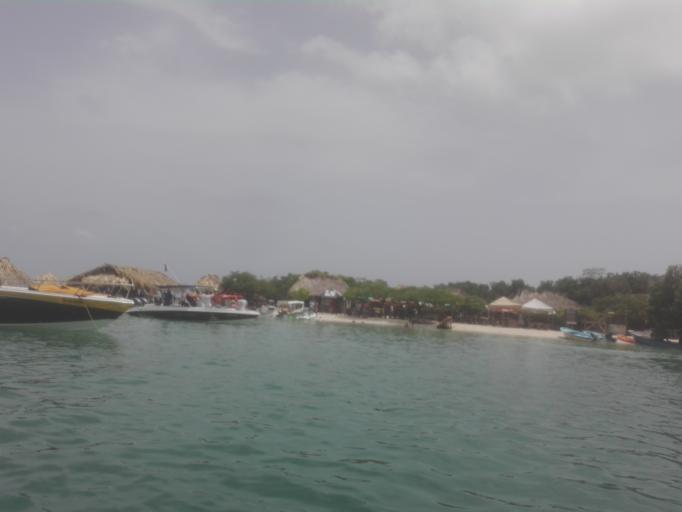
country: CO
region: Bolivar
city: Turbana
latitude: 10.1638
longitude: -75.6688
